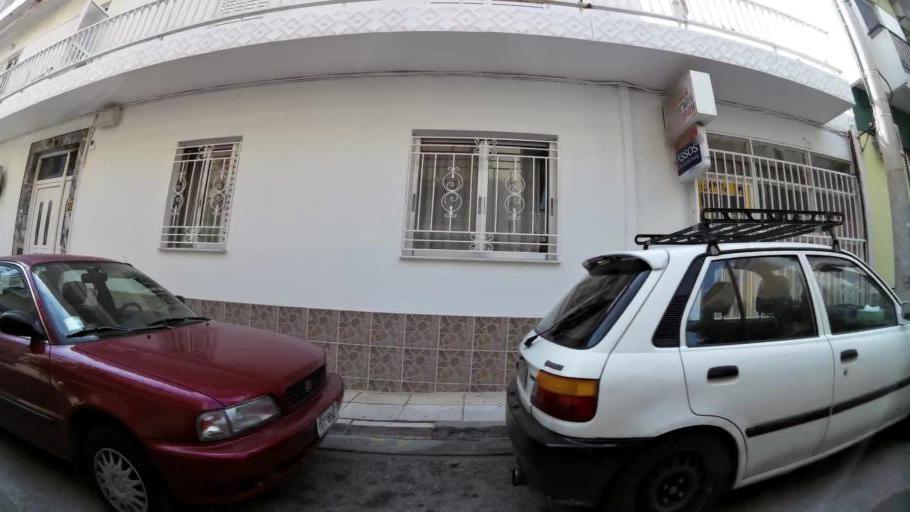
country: GR
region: Attica
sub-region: Nomarchia Athinas
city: Chaidari
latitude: 38.0207
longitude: 23.6759
